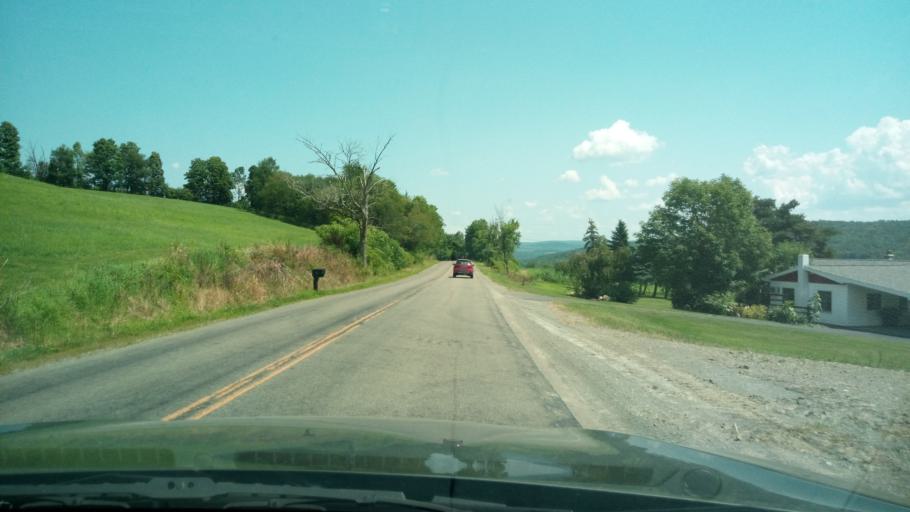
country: US
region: New York
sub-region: Schuyler County
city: Montour Falls
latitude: 42.2920
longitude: -76.7903
